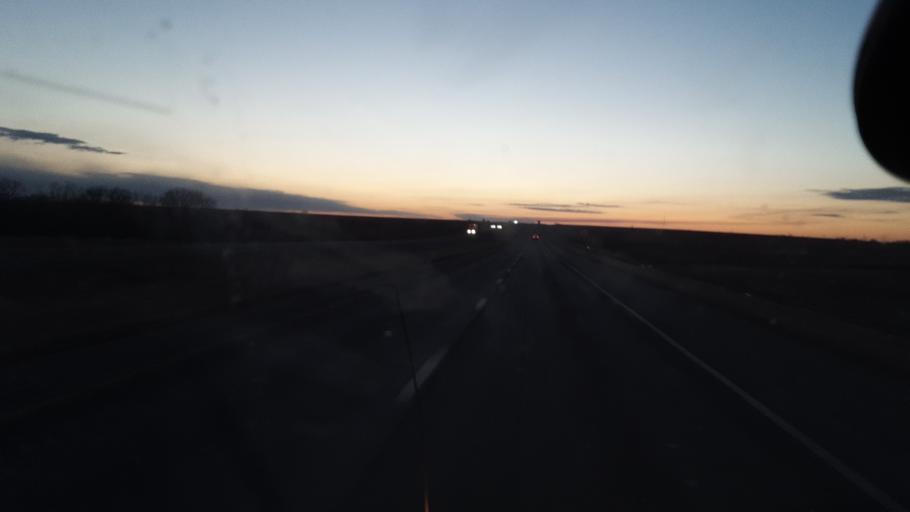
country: US
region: Kansas
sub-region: Osage County
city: Lyndon
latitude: 38.4265
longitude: -95.7880
